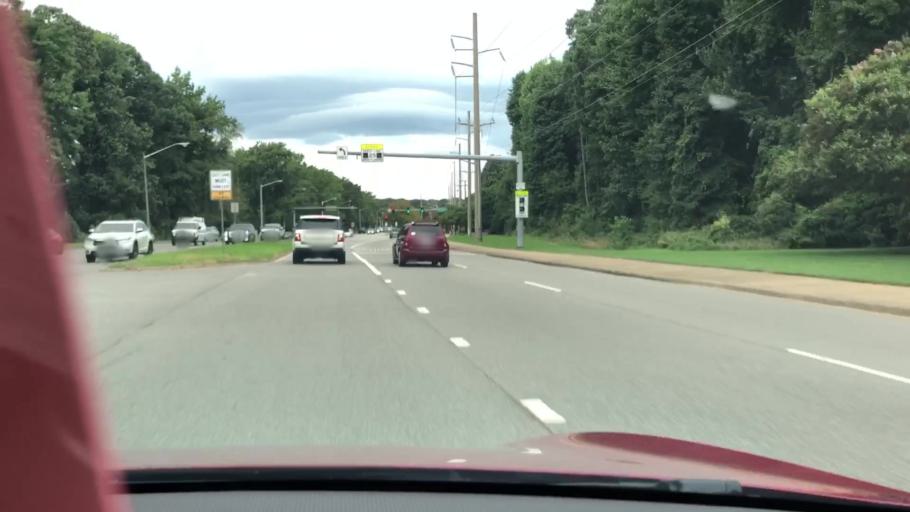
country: US
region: Virginia
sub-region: City of Virginia Beach
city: Virginia Beach
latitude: 36.8848
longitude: -76.0477
